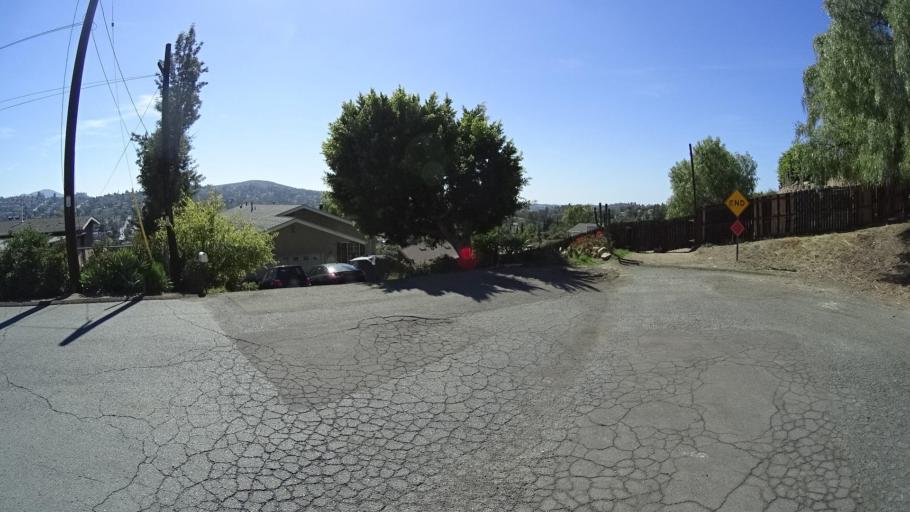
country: US
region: California
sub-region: San Diego County
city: Casa de Oro-Mount Helix
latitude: 32.7553
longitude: -116.9837
